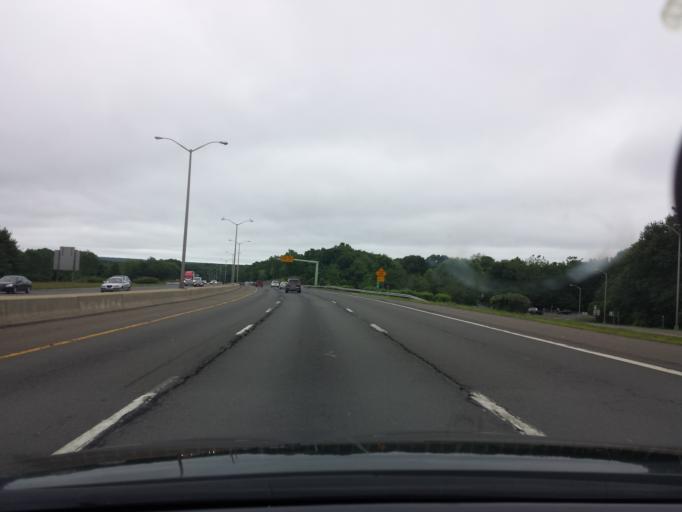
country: US
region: Connecticut
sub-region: Middlesex County
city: Old Saybrook Center
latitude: 41.3199
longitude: -72.3416
